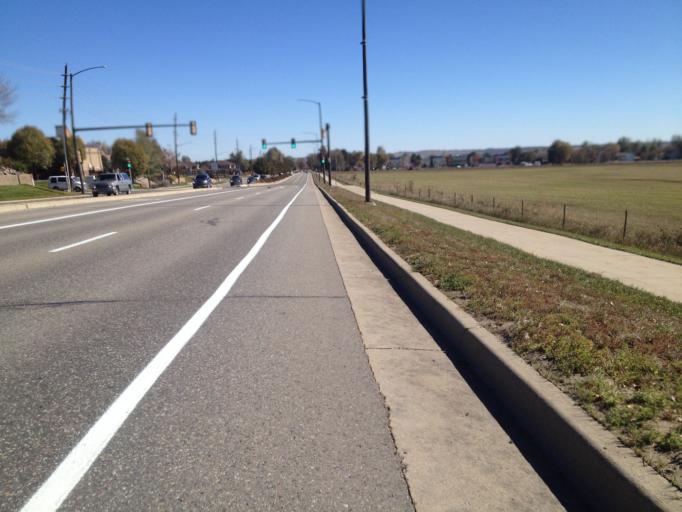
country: US
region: Colorado
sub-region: Boulder County
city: Louisville
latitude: 39.9868
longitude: -105.1243
